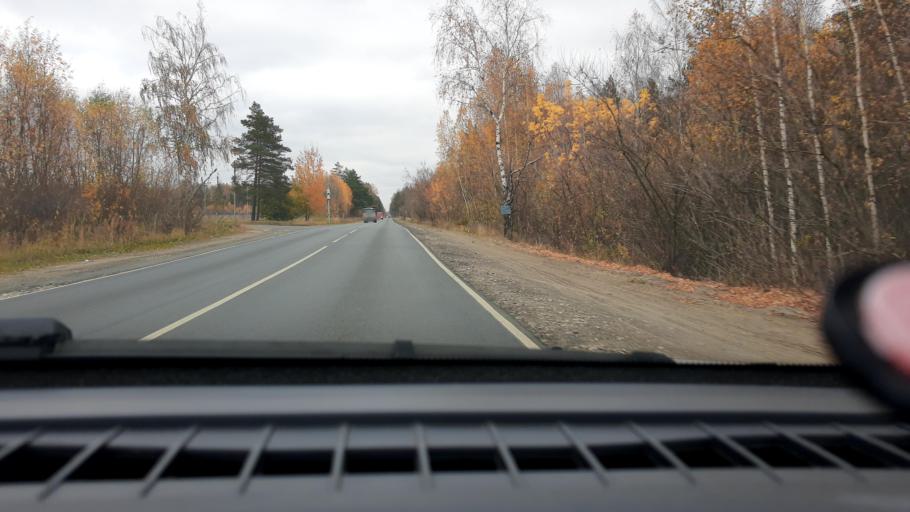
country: RU
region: Nizjnij Novgorod
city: Babino
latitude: 56.2603
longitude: 43.6710
